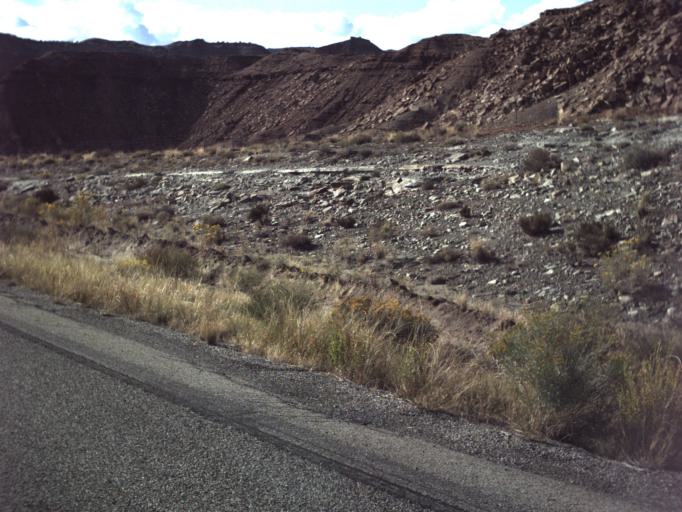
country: US
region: Utah
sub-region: Emery County
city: Ferron
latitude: 38.8311
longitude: -111.1183
